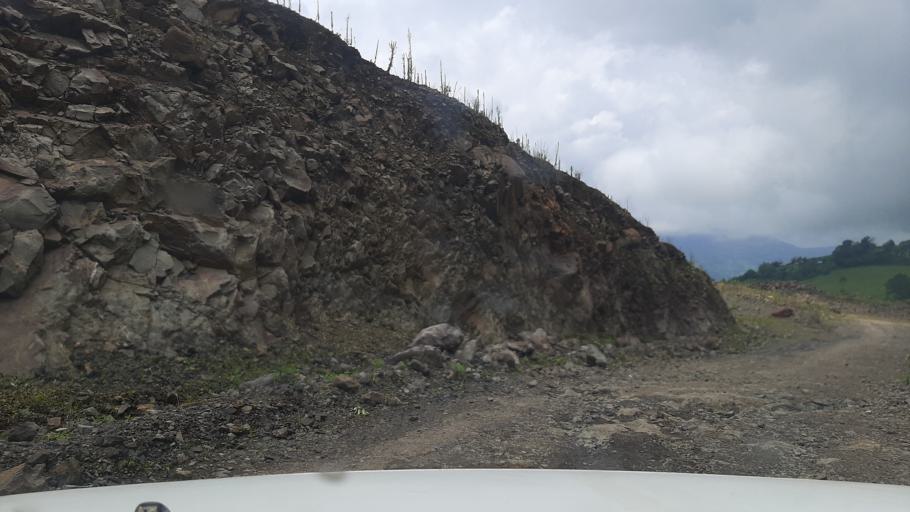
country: ET
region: Southern Nations, Nationalities, and People's Region
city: Bonga
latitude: 7.1340
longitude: 36.5580
